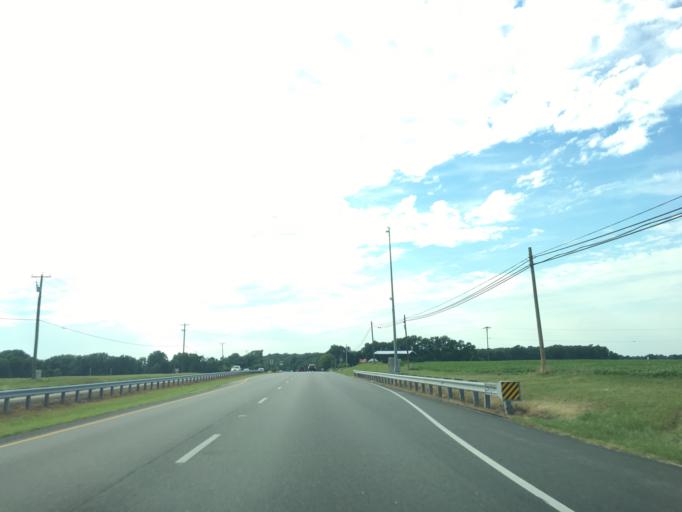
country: US
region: Maryland
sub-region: Queen Anne's County
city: Grasonville
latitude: 38.9714
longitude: -76.1220
